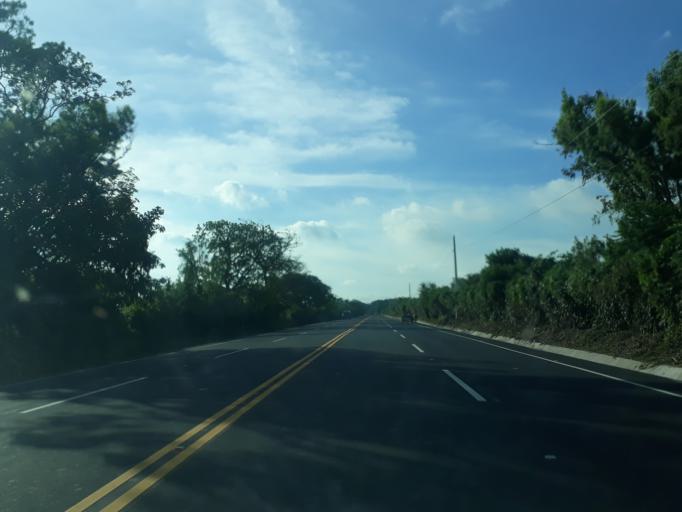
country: NI
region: Carazo
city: Diriamba
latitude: 11.9096
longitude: -86.2652
